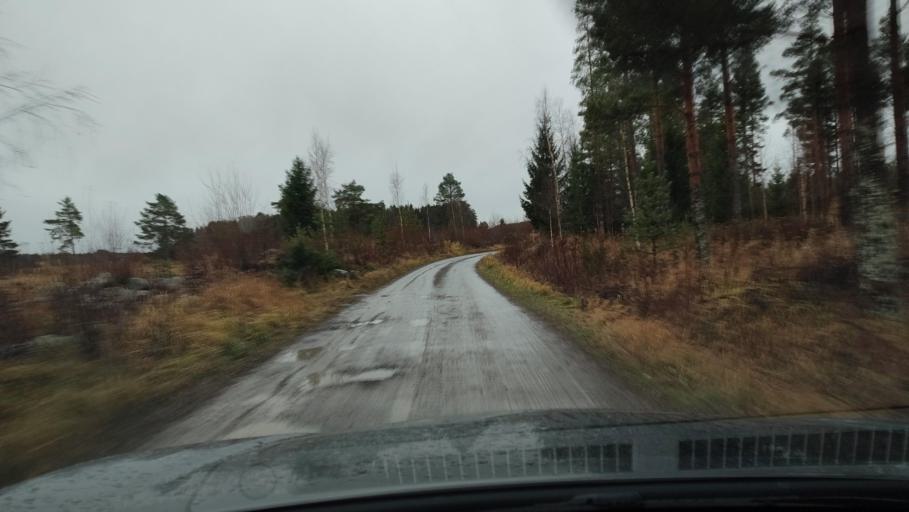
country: FI
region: Southern Ostrobothnia
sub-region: Suupohja
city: Karijoki
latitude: 62.2355
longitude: 21.5497
